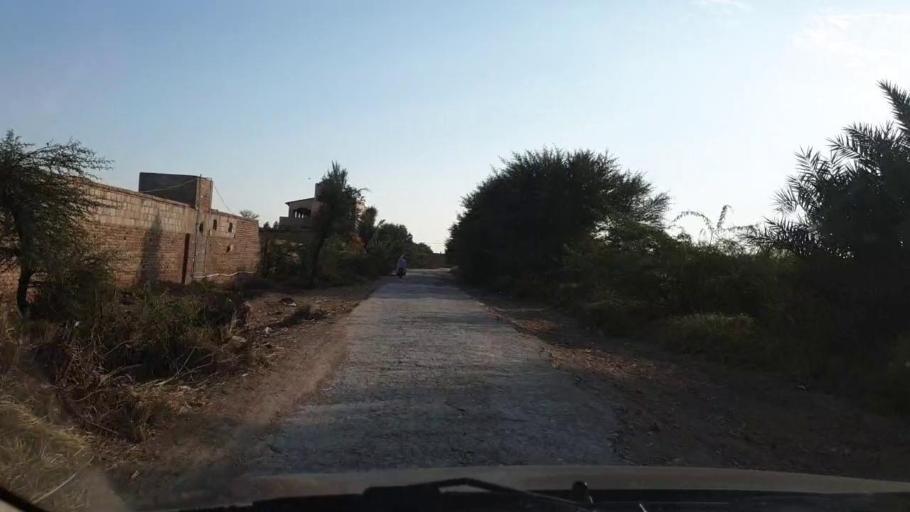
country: PK
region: Sindh
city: Jhol
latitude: 25.9511
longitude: 68.8615
